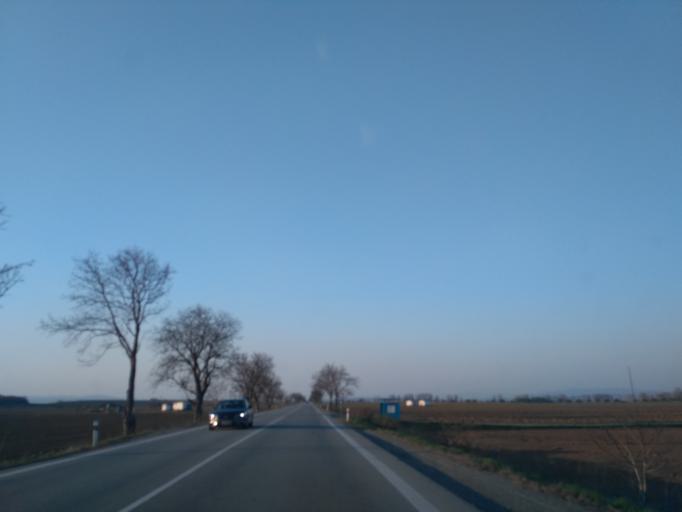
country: HU
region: Borsod-Abauj-Zemplen
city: Gonc
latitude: 48.5789
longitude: 21.2585
